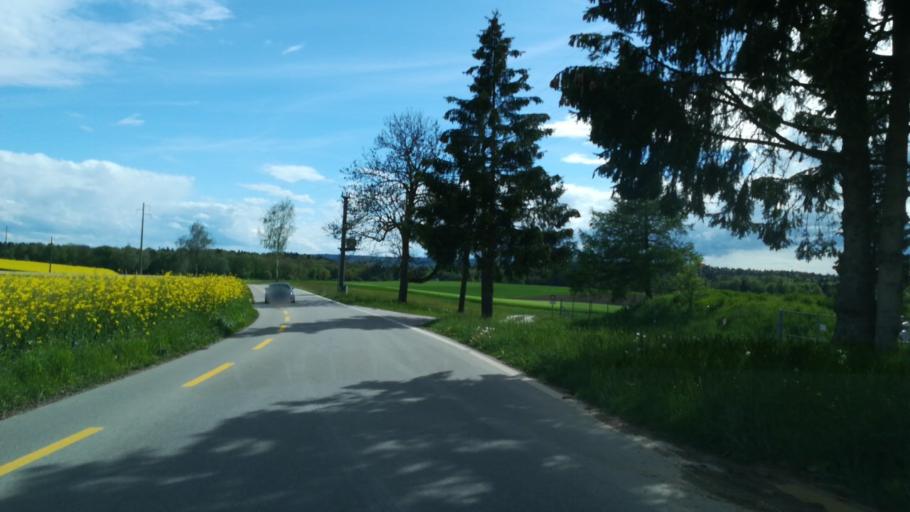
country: CH
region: Schaffhausen
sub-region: Bezirk Reiat
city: Thayngen
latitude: 47.7299
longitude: 8.7109
